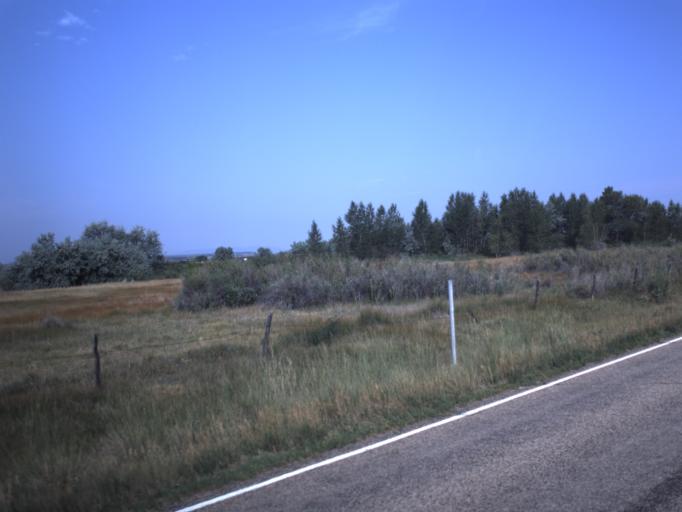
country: US
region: Utah
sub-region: Duchesne County
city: Duchesne
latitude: 40.3251
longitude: -110.2639
